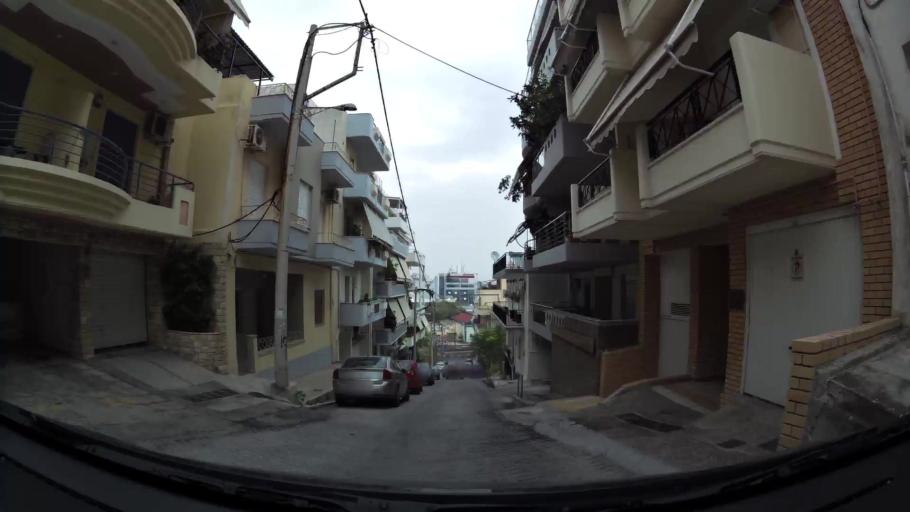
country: GR
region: Attica
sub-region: Nomos Attikis
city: Piraeus
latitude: 37.9476
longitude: 23.6532
